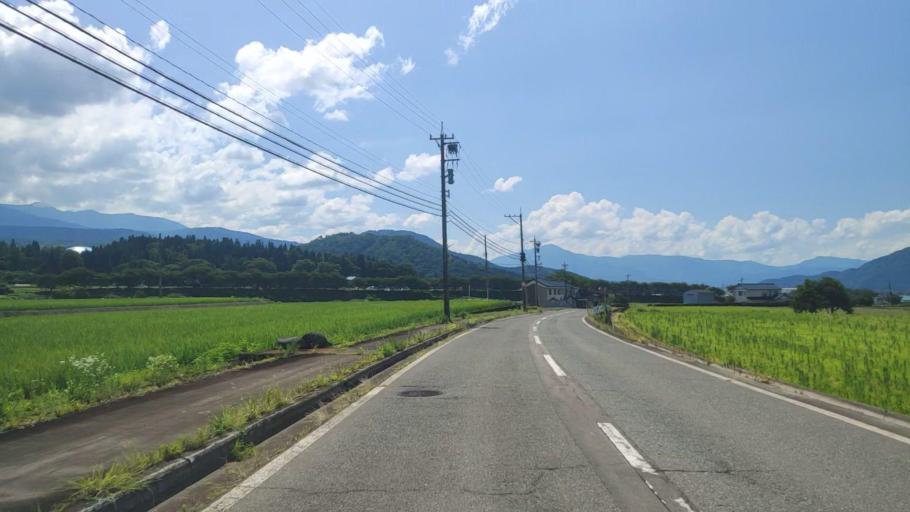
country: JP
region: Fukui
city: Katsuyama
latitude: 36.0866
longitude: 136.4939
